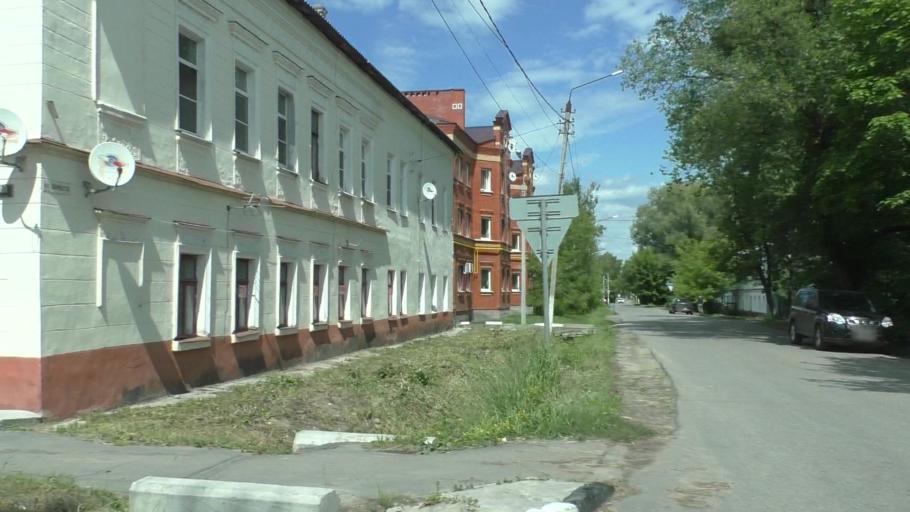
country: RU
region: Moskovskaya
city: Yegor'yevsk
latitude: 55.3851
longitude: 39.0363
